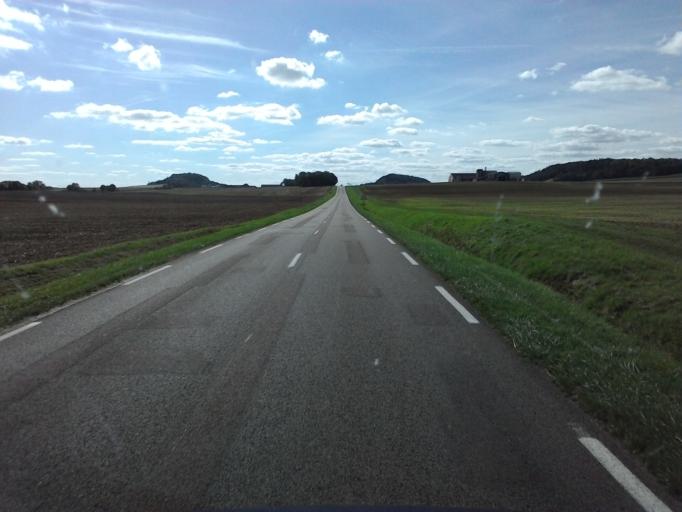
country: FR
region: Bourgogne
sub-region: Departement de la Cote-d'Or
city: Chatillon-sur-Seine
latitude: 47.9093
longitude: 4.6348
